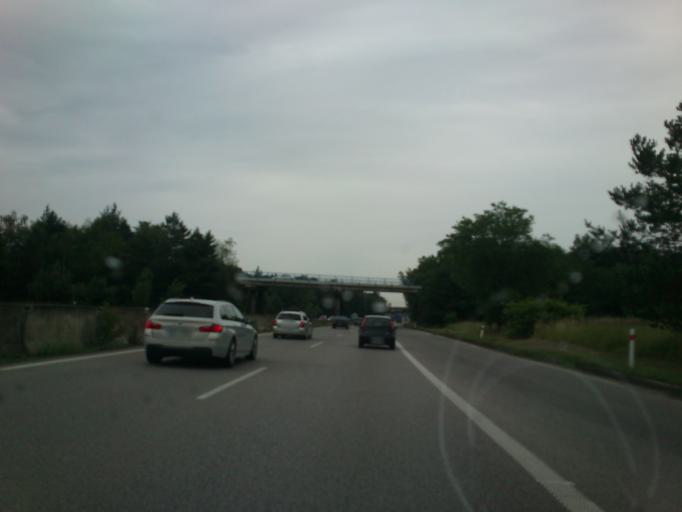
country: CZ
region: Central Bohemia
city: Brandys nad Labem-Stara Boleslav
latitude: 50.2032
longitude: 14.6928
